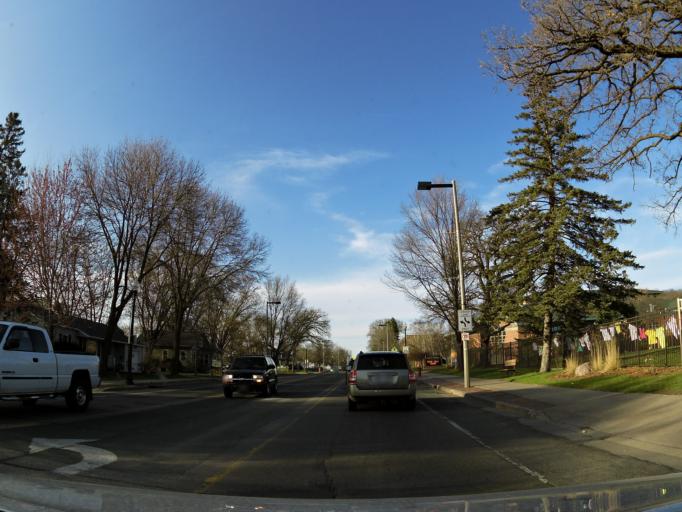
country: US
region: Wisconsin
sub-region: Pierce County
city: River Falls
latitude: 44.8633
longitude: -92.6235
